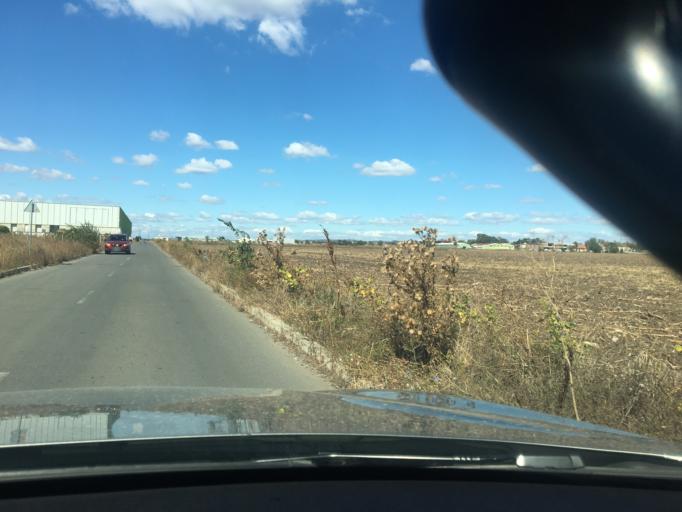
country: BG
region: Burgas
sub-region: Obshtina Burgas
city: Burgas
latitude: 42.5323
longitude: 27.4547
